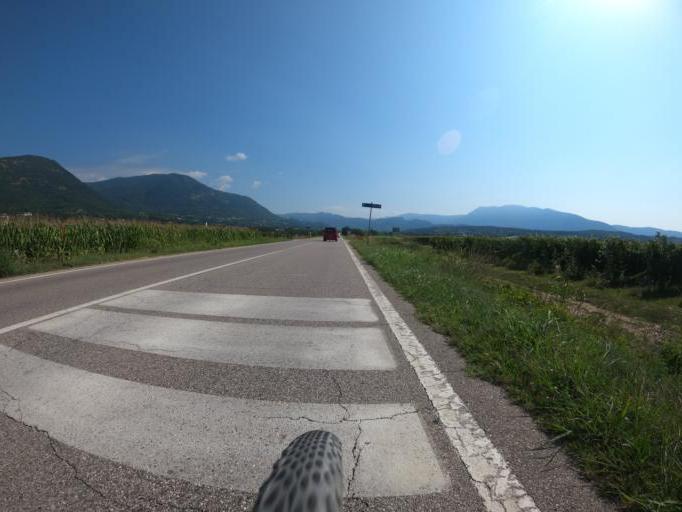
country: IT
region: Veneto
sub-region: Provincia di Verona
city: Costermano
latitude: 45.5903
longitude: 10.7564
